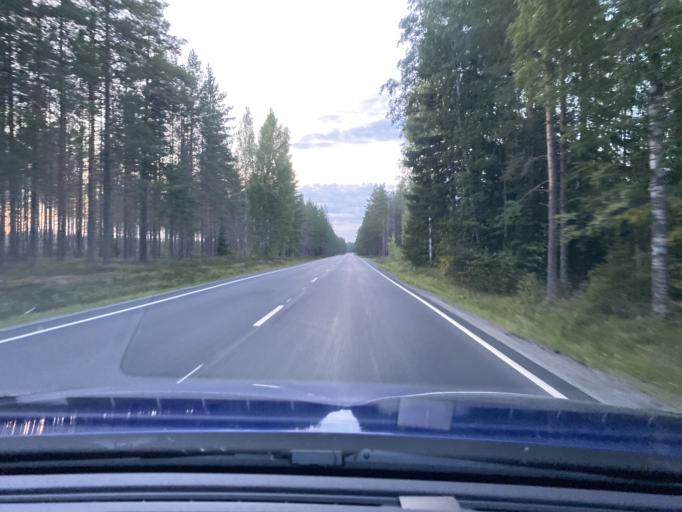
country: FI
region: Satakunta
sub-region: Pohjois-Satakunta
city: Honkajoki
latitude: 62.0574
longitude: 22.2503
